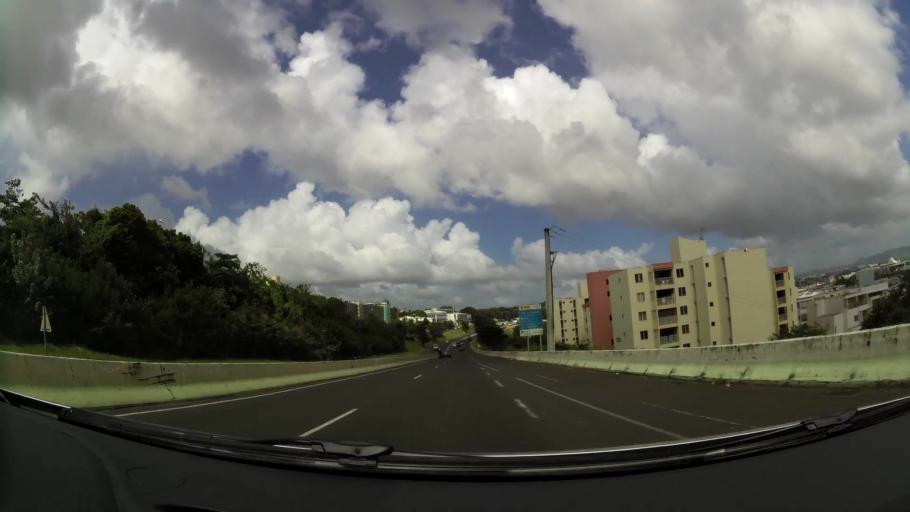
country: MQ
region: Martinique
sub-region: Martinique
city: Fort-de-France
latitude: 14.6132
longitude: -61.0418
